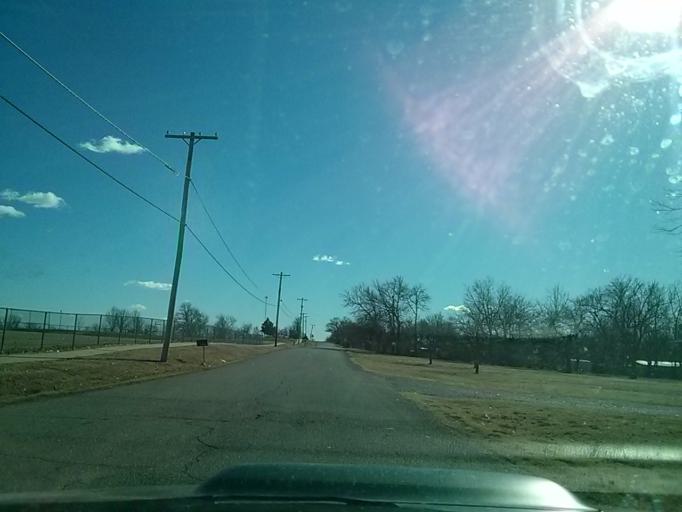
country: US
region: Oklahoma
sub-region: Tulsa County
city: Turley
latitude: 36.2126
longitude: -95.9515
